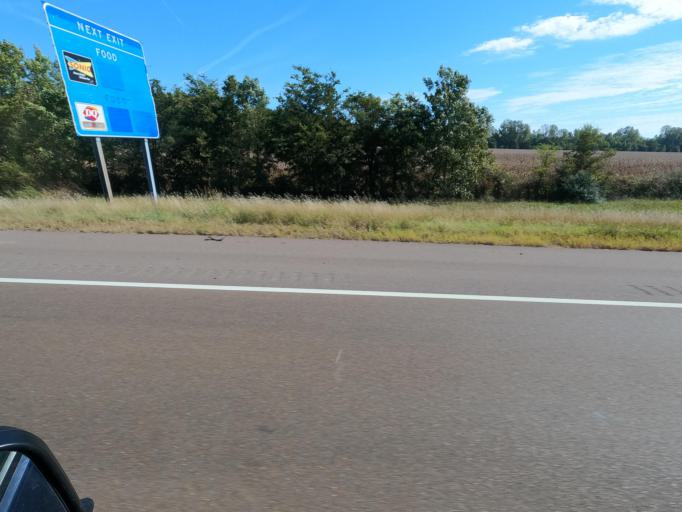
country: US
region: Tennessee
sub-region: Dyer County
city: Dyersburg
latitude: 36.0460
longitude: -89.3357
